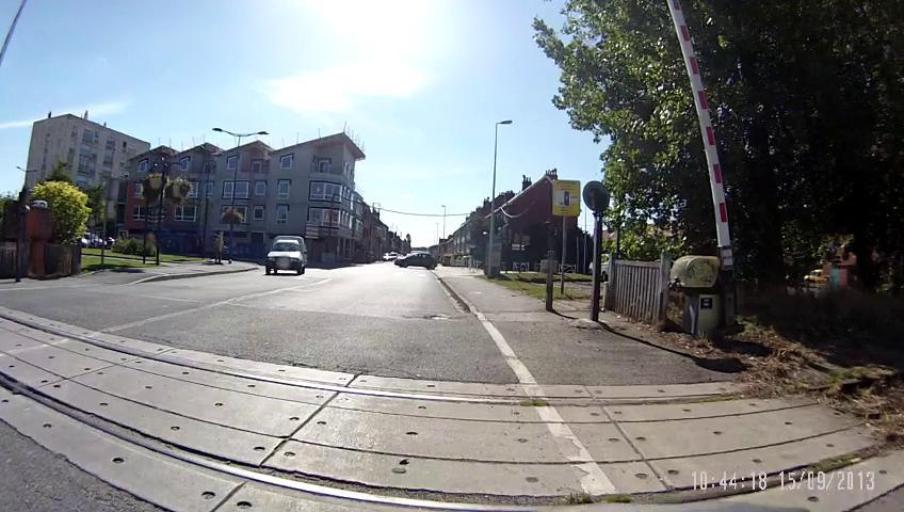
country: FR
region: Nord-Pas-de-Calais
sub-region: Departement du Nord
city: Teteghem
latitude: 51.0506
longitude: 2.4319
